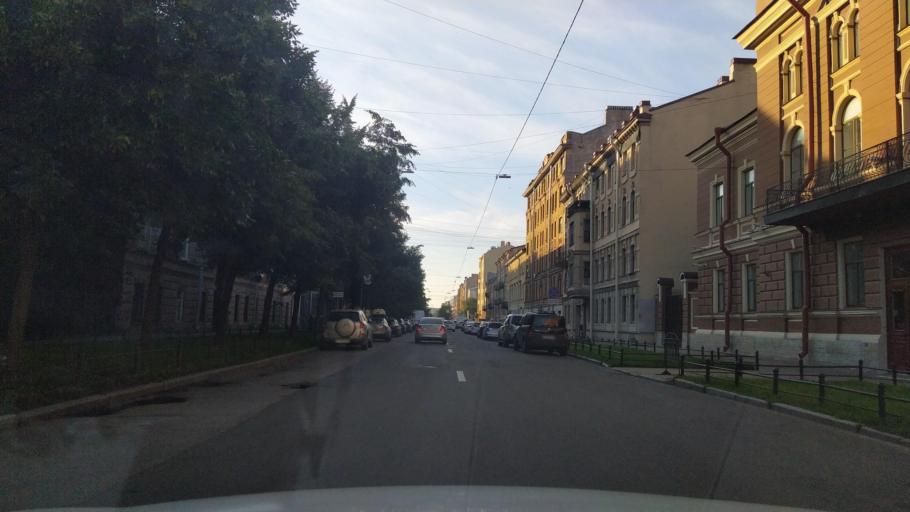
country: RU
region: St.-Petersburg
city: Vasyl'evsky Ostrov
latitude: 59.9326
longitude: 30.2705
